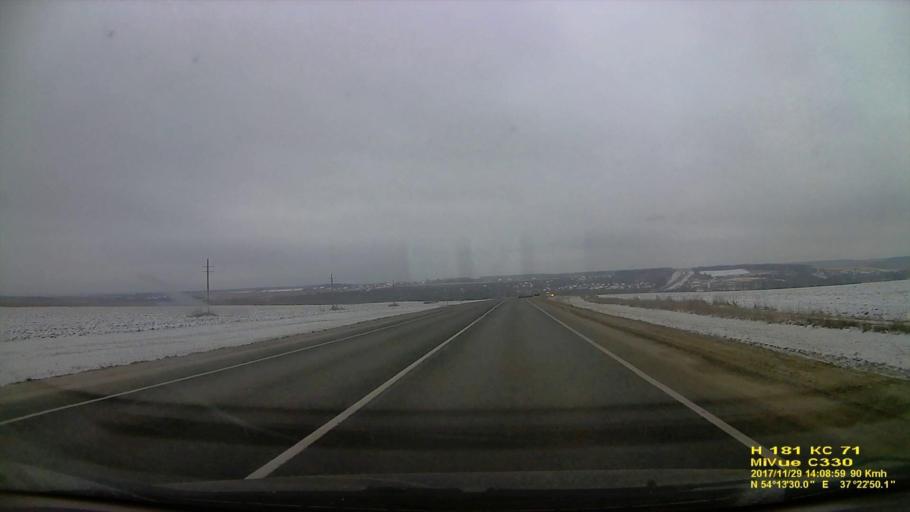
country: RU
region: Tula
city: Leninskiy
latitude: 54.2248
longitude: 37.3811
